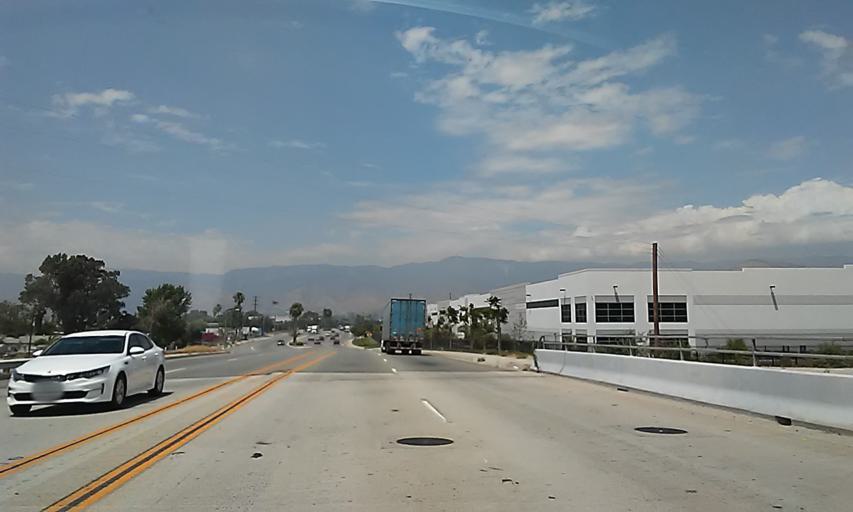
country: US
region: California
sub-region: San Bernardino County
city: Loma Linda
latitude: 34.0827
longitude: -117.2595
